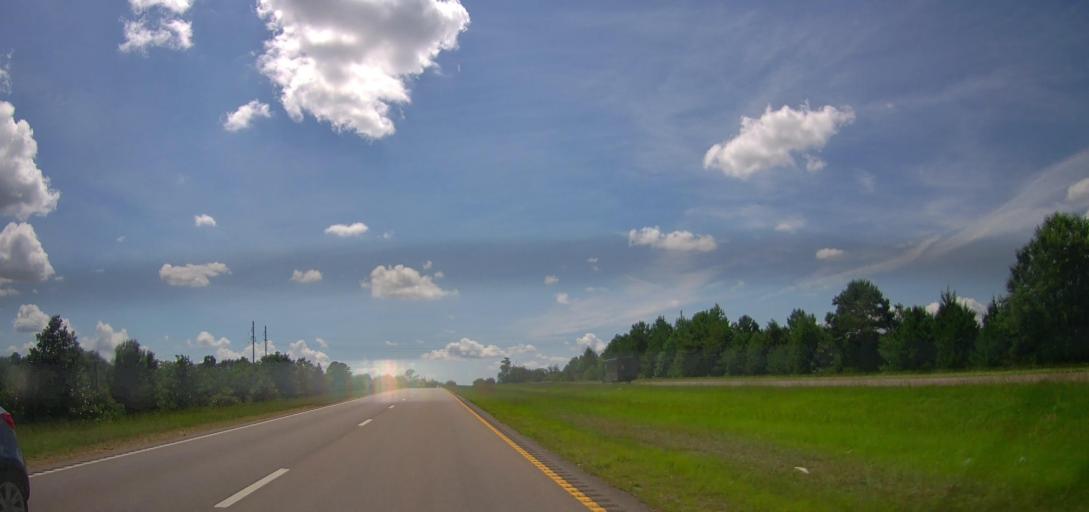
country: US
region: Mississippi
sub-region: Monroe County
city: Aberdeen
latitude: 33.8157
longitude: -88.5352
